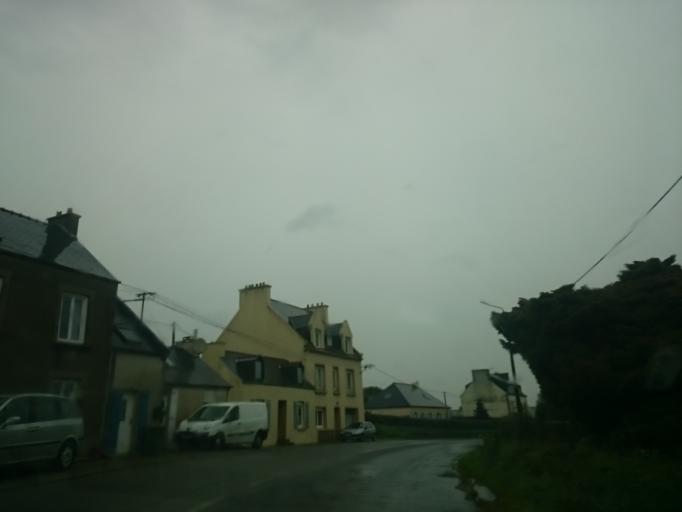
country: FR
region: Brittany
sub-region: Departement du Finistere
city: Le Drennec
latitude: 48.5326
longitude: -4.3741
